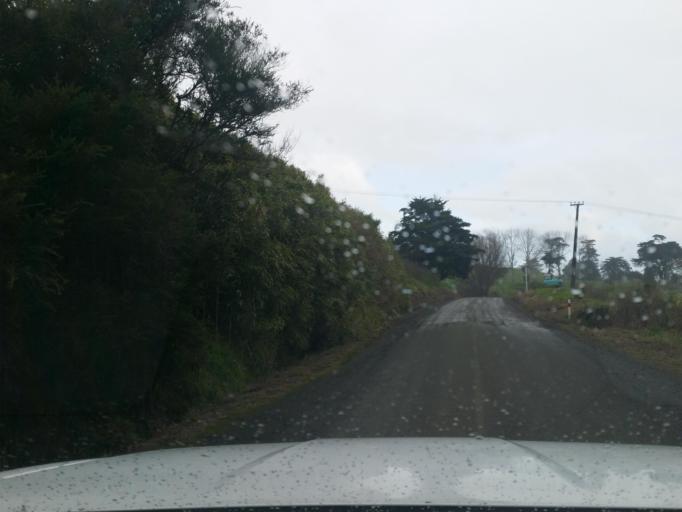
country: NZ
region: Northland
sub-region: Kaipara District
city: Dargaville
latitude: -35.8230
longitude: 173.7845
